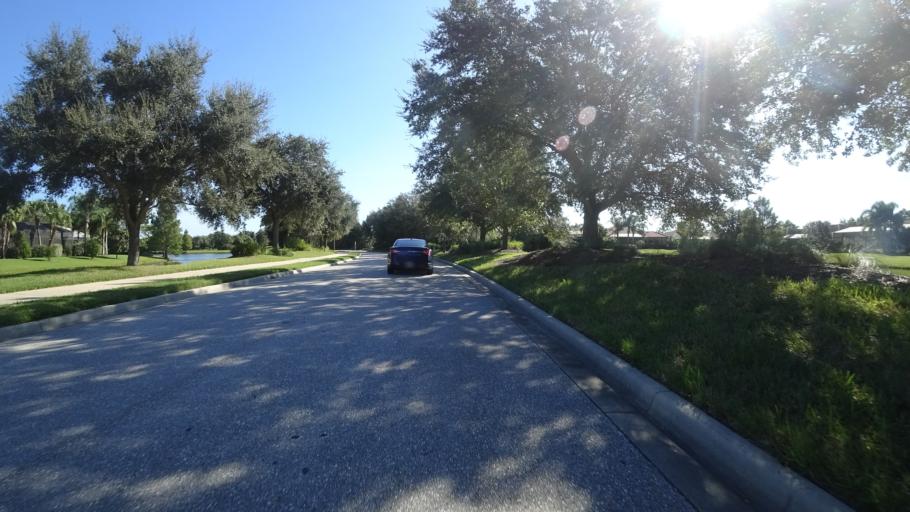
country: US
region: Florida
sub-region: Sarasota County
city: The Meadows
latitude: 27.4086
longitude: -82.4040
